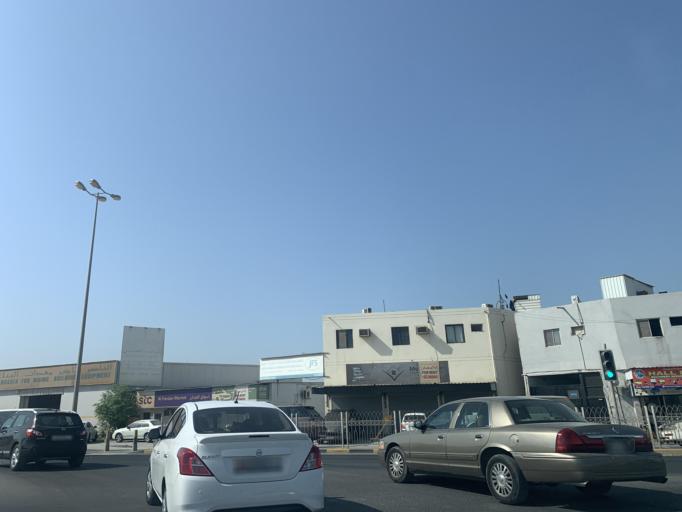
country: BH
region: Central Governorate
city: Madinat Hamad
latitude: 26.1394
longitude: 50.4884
